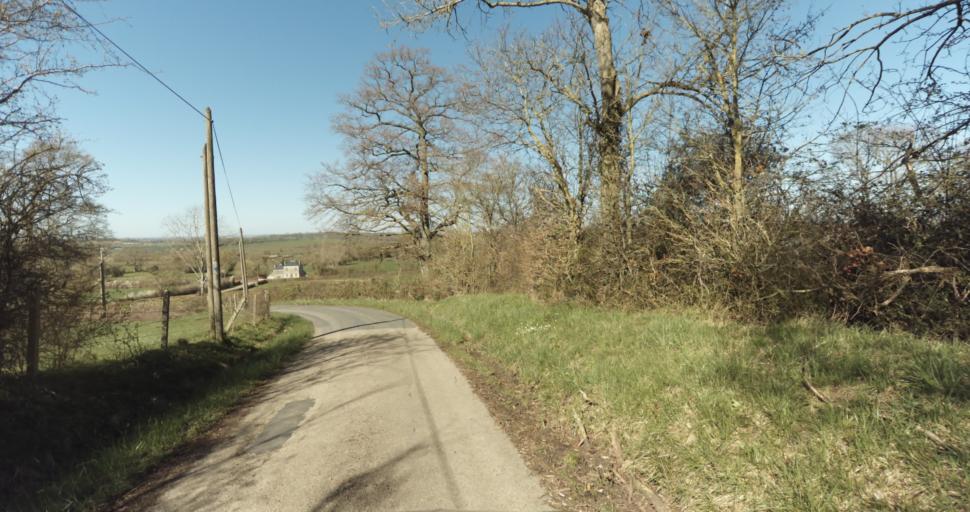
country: FR
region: Lower Normandy
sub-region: Departement de l'Orne
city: Trun
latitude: 48.9481
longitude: 0.0487
